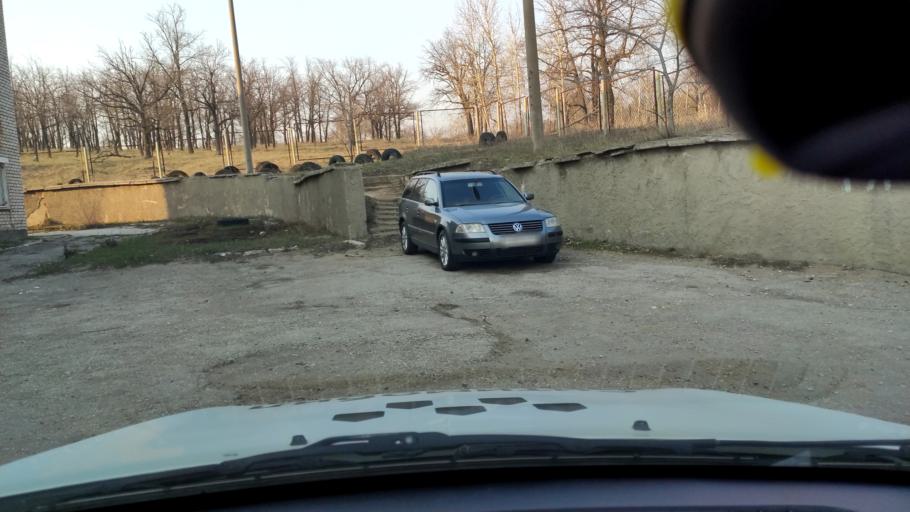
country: RU
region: Samara
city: Zhigulevsk
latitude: 53.4772
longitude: 49.5391
